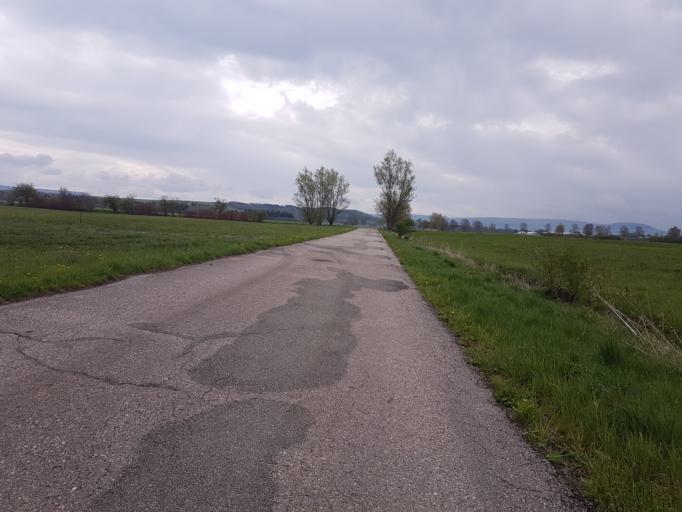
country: DE
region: Baden-Wuerttemberg
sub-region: Freiburg Region
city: Donaueschingen
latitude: 47.9642
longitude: 8.5203
